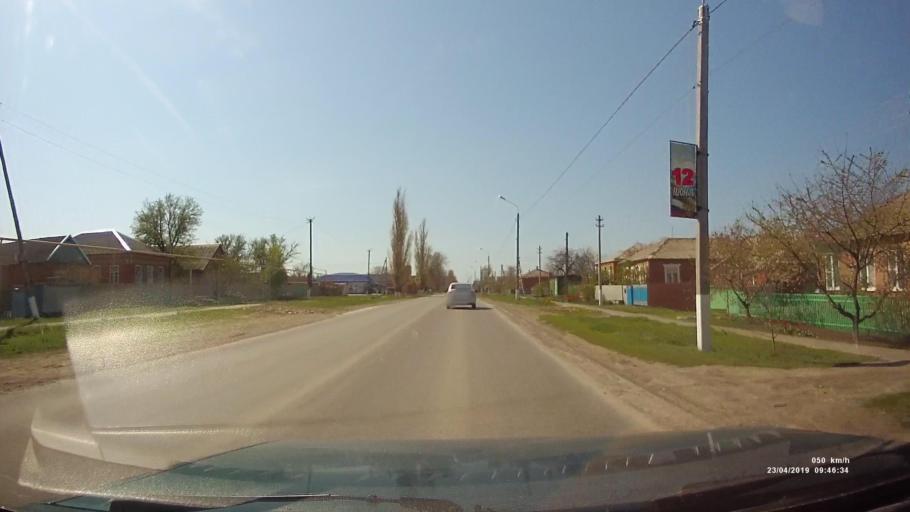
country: RU
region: Rostov
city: Orlovskiy
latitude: 46.8812
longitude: 42.0384
